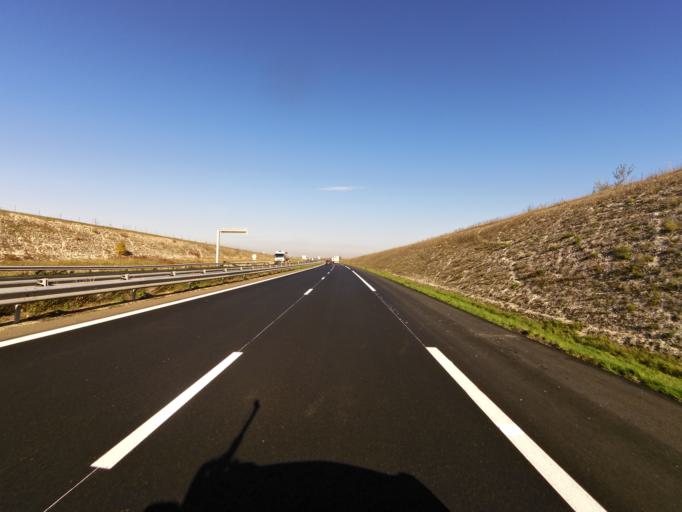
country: FR
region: Champagne-Ardenne
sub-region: Departement de la Marne
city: Fagnieres
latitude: 48.9531
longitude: 4.2897
